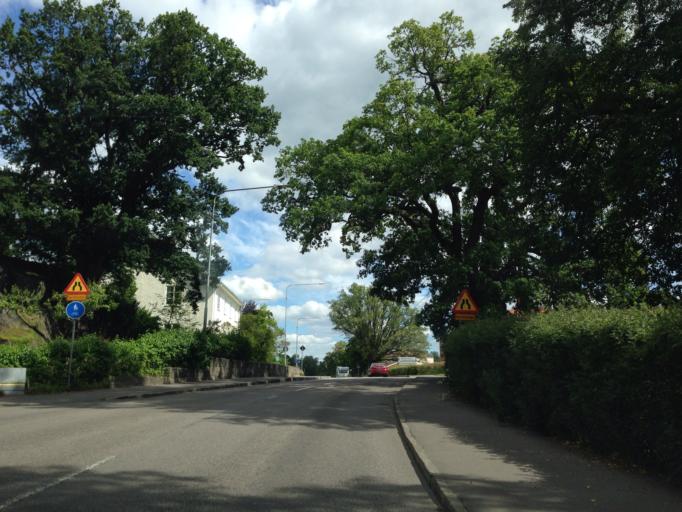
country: SE
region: OEstergoetland
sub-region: Kinda Kommun
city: Kisa
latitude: 57.9917
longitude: 15.6360
